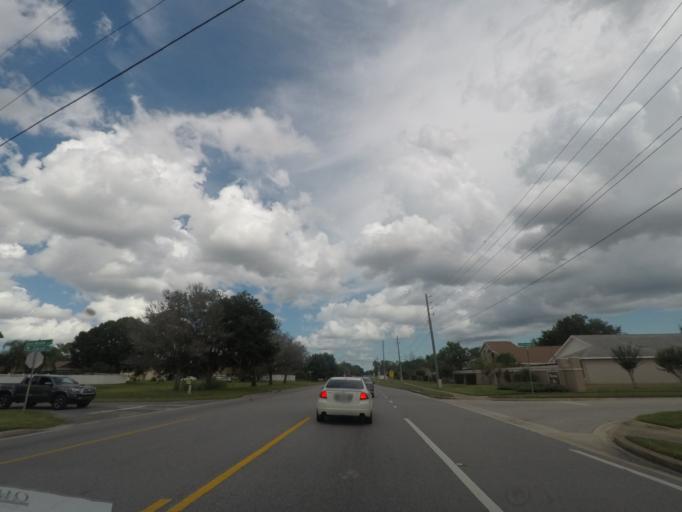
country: US
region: Florida
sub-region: Osceola County
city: Kissimmee
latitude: 28.3261
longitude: -81.4135
